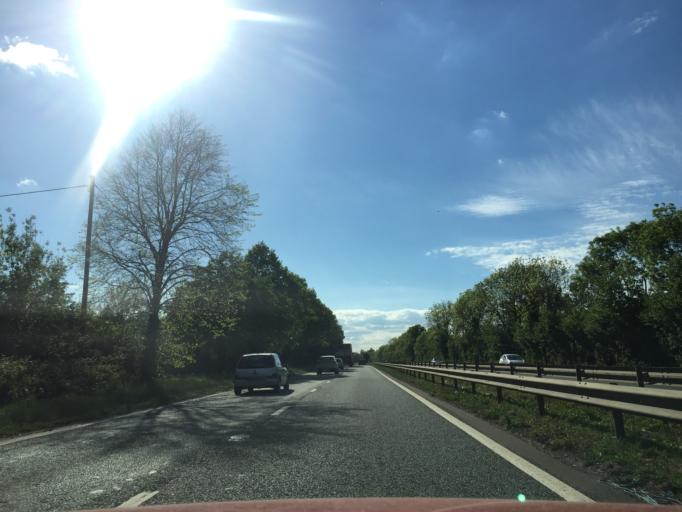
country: GB
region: England
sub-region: Warwickshire
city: Wolston
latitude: 52.3501
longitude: -1.3614
